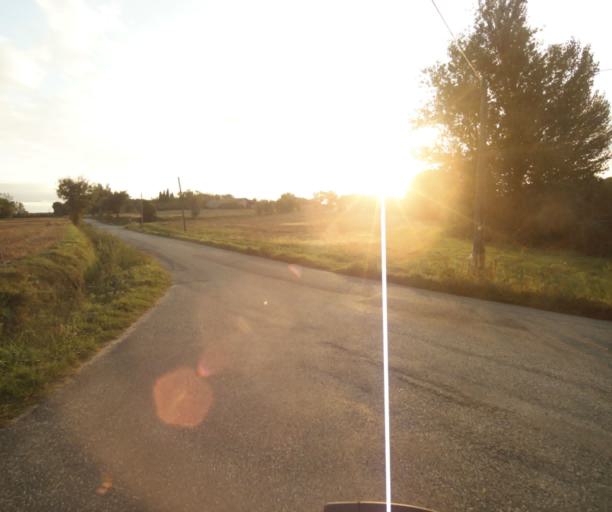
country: FR
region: Midi-Pyrenees
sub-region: Departement du Tarn-et-Garonne
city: Verdun-sur-Garonne
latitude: 43.8295
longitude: 1.1915
